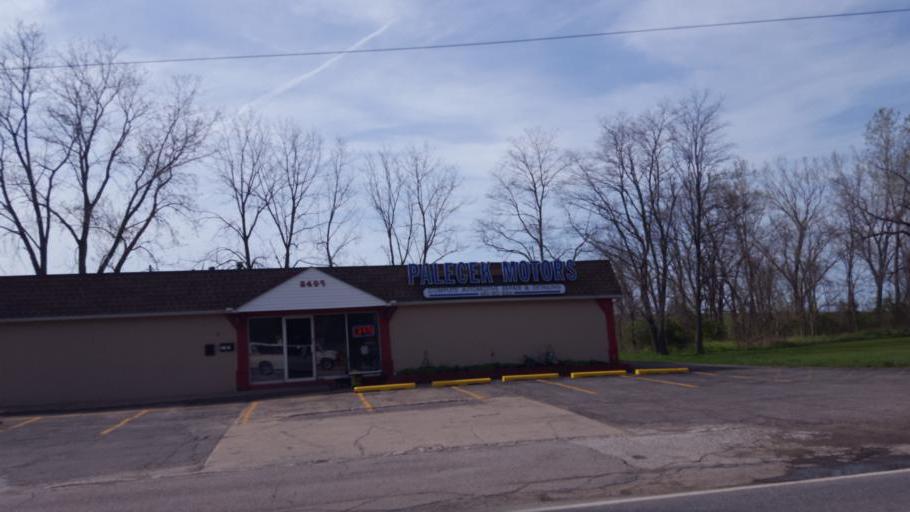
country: US
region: Ohio
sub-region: Lake County
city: Perry
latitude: 41.7590
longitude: -81.1917
